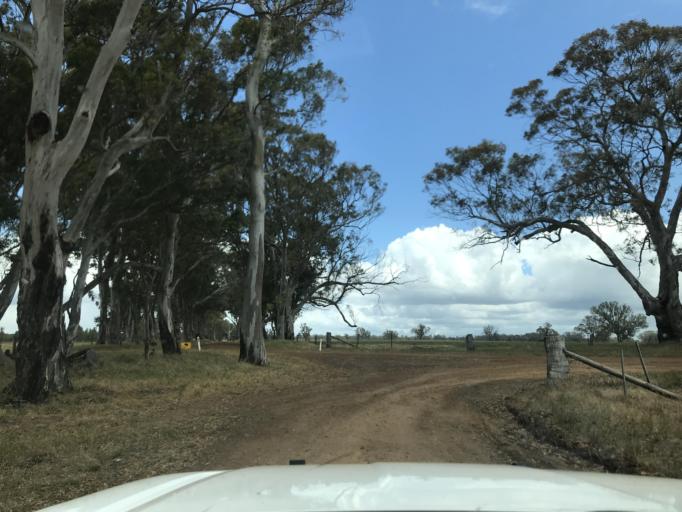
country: AU
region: South Australia
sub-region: Wattle Range
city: Penola
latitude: -37.1031
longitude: 141.3191
